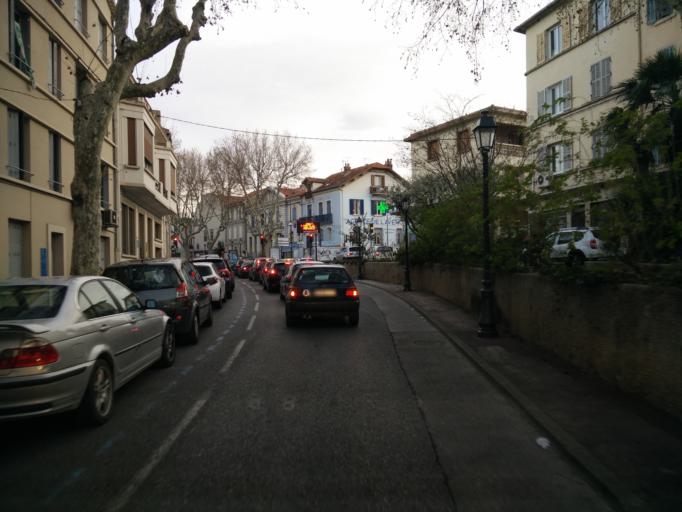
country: FR
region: Provence-Alpes-Cote d'Azur
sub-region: Departement du Var
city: La Seyne-sur-Mer
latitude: 43.1000
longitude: 5.8826
